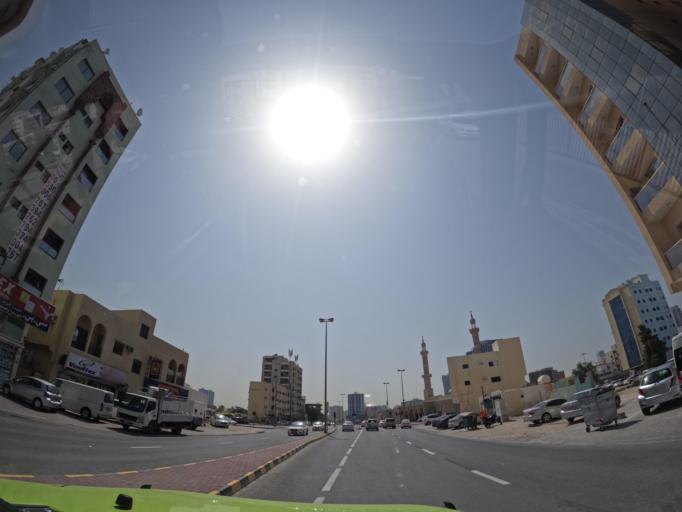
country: AE
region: Ajman
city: Ajman
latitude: 25.4157
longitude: 55.4468
